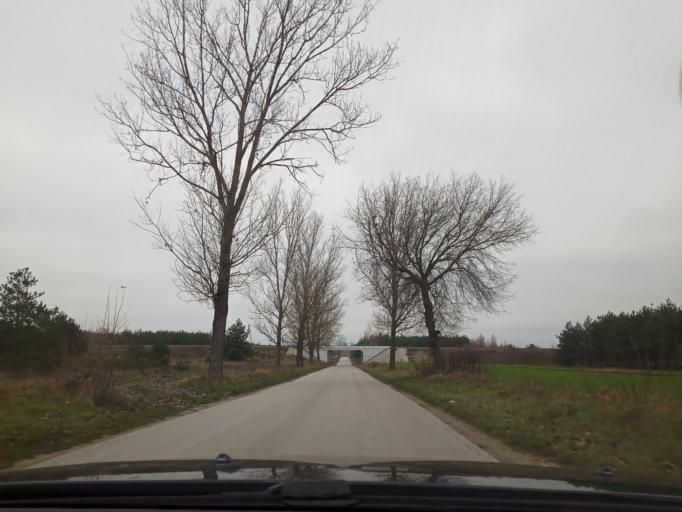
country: PL
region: Swietokrzyskie
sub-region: Powiat jedrzejowski
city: Imielno
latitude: 50.5958
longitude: 20.4820
